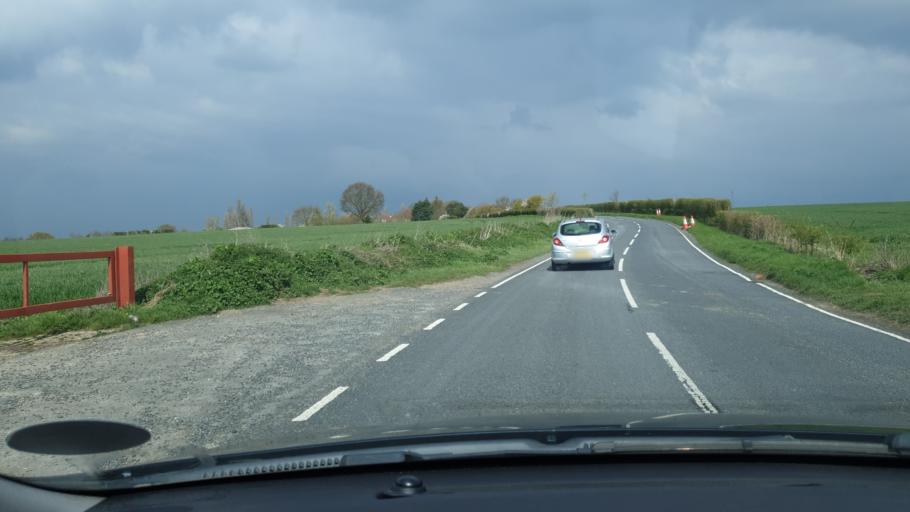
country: GB
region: England
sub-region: Essex
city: Mistley
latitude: 51.8978
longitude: 1.0912
